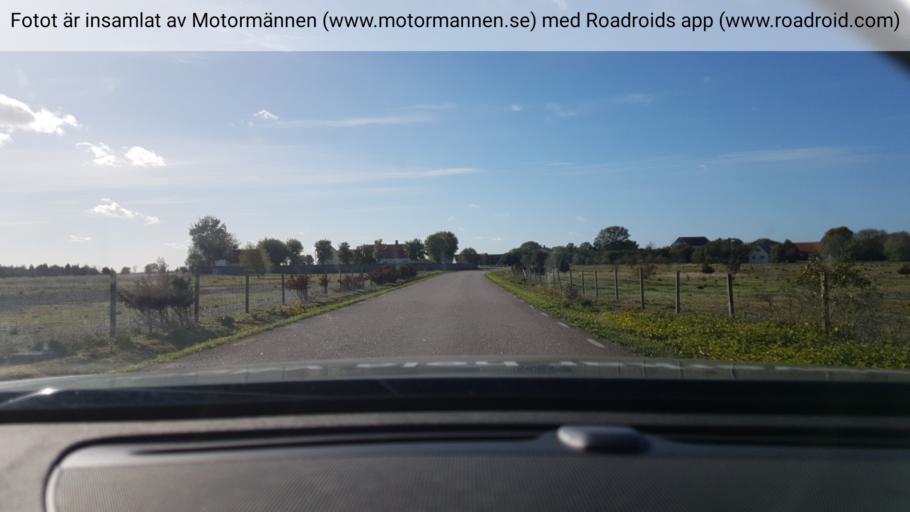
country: SE
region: Gotland
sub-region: Gotland
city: Slite
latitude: 57.9150
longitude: 18.9462
